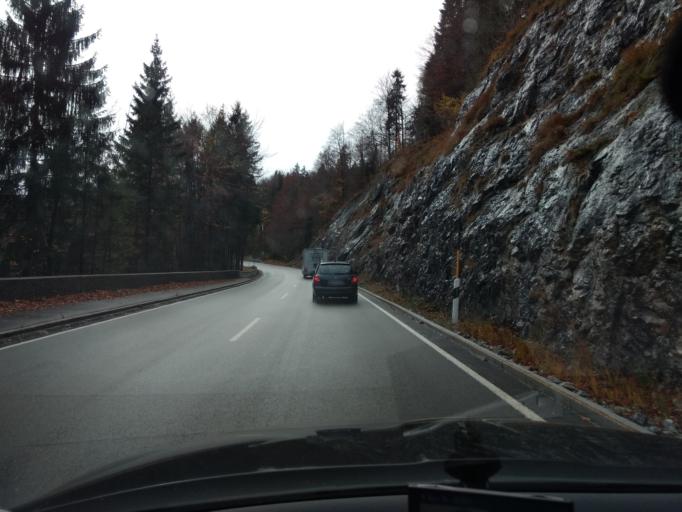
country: DE
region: Bavaria
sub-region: Upper Bavaria
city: Lenggries
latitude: 47.5831
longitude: 11.5471
